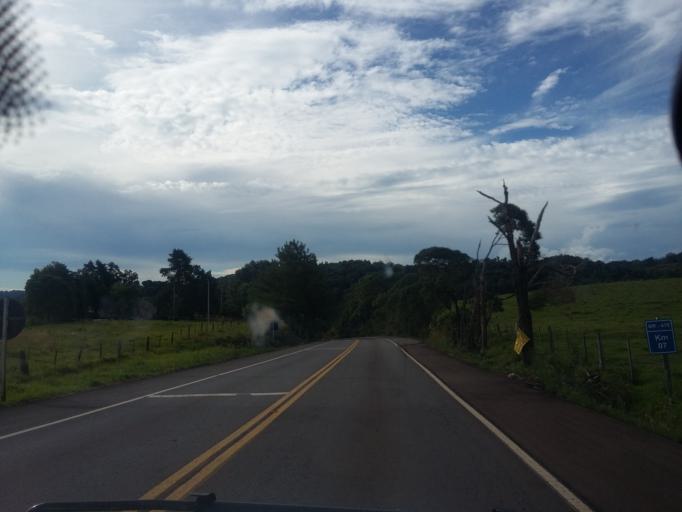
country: BR
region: Santa Catarina
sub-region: Celso Ramos
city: Celso Ramos
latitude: -27.6245
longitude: -51.4709
